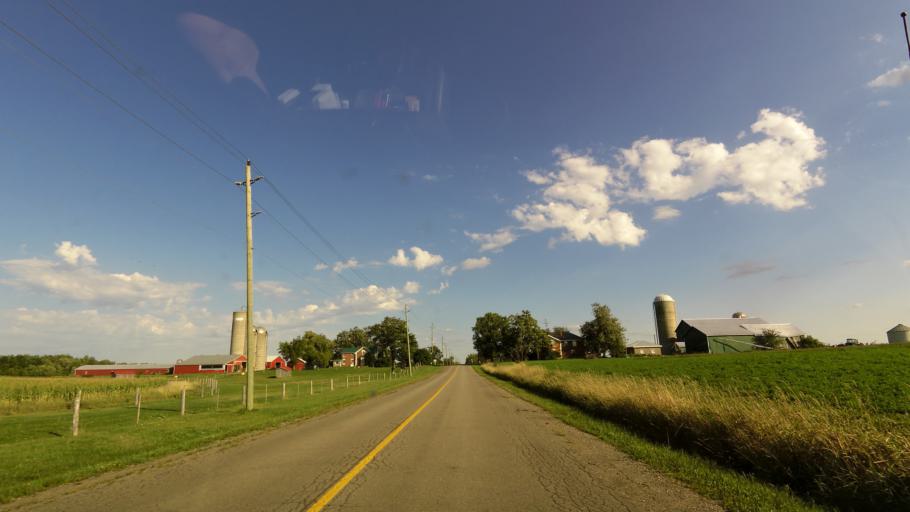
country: CA
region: Ontario
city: Brampton
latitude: 43.7530
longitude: -79.8988
